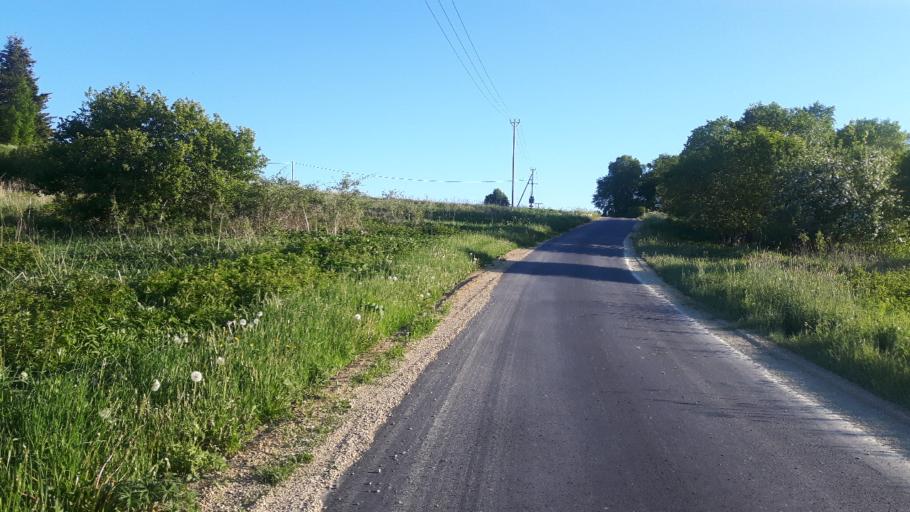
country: EE
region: Ida-Virumaa
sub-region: Kivioli linn
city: Kivioli
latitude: 59.4307
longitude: 26.9572
